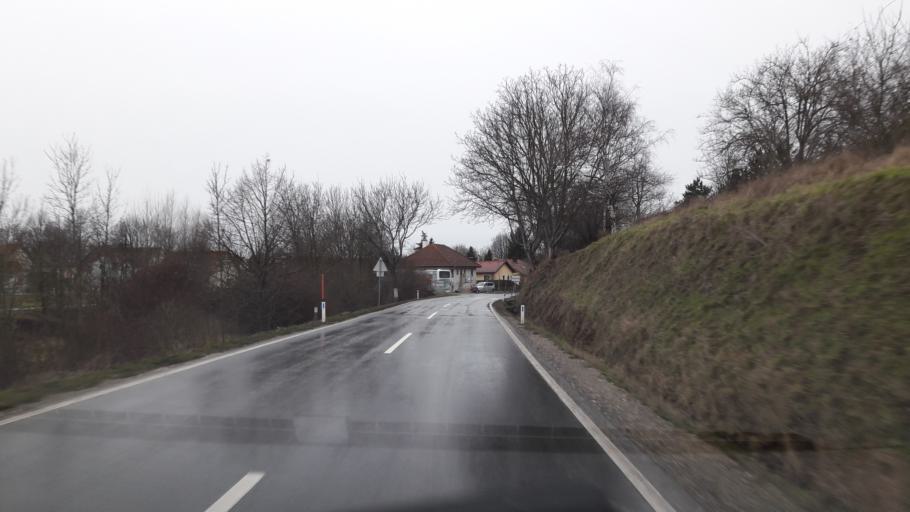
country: AT
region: Lower Austria
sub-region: Politischer Bezirk Mistelbach
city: Hochleithen
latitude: 48.4429
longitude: 16.5326
